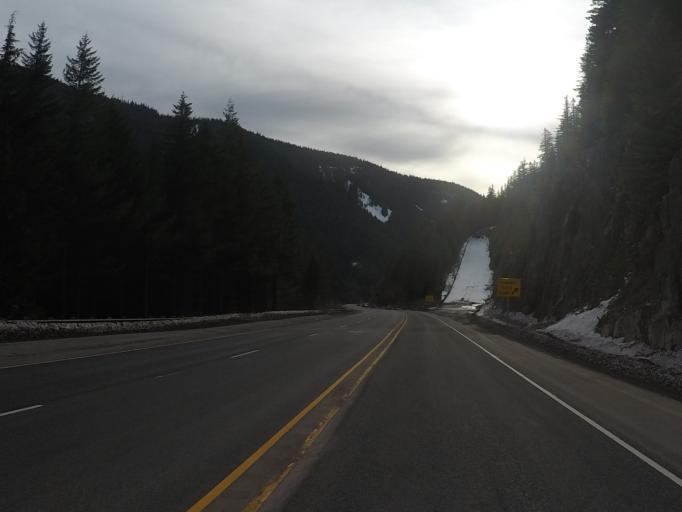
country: US
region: Oregon
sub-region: Clackamas County
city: Mount Hood Village
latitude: 45.3064
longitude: -121.8139
